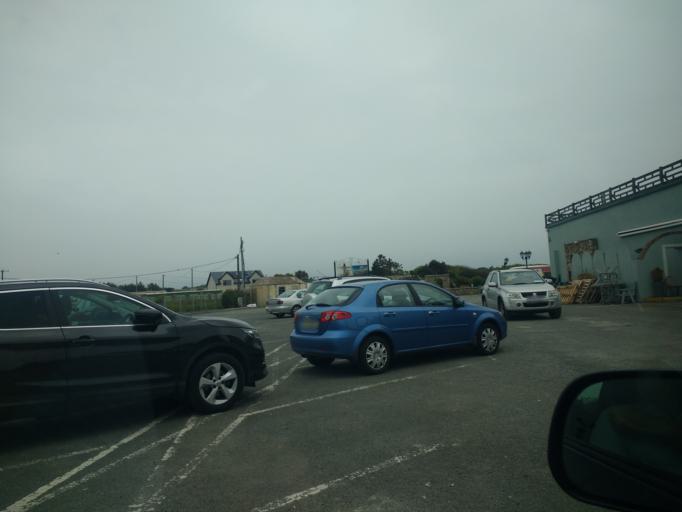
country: IE
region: Leinster
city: Portraine
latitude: 53.4790
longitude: -6.1156
